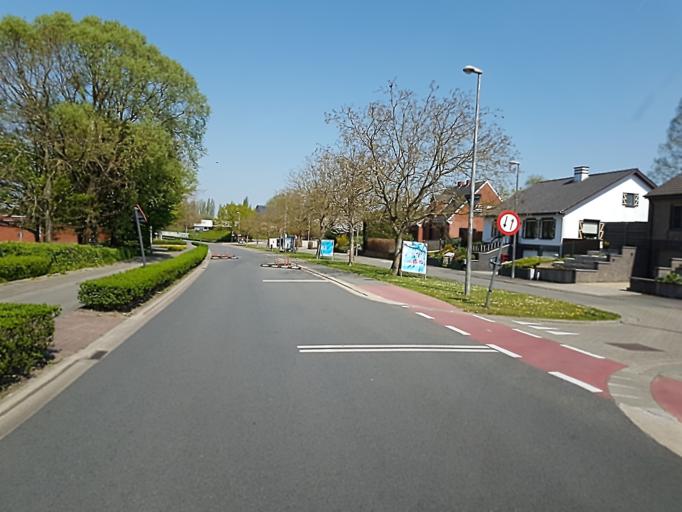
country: BE
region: Flanders
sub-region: Provincie West-Vlaanderen
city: Kortrijk
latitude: 50.8060
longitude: 3.2435
